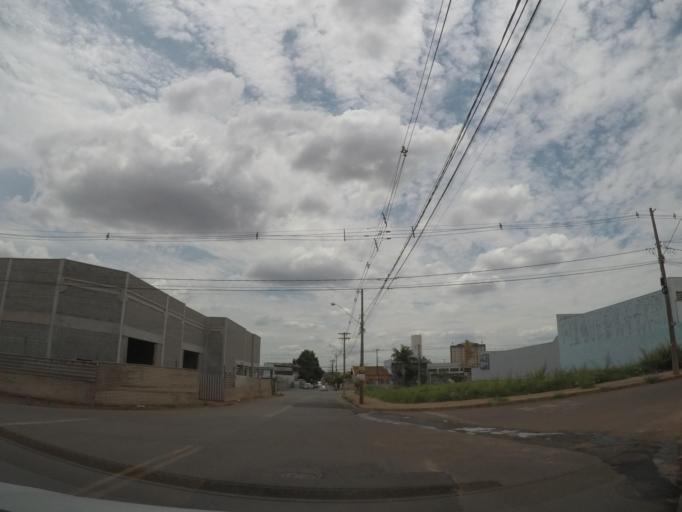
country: BR
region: Sao Paulo
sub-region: Sumare
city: Sumare
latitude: -22.8345
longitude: -47.2728
